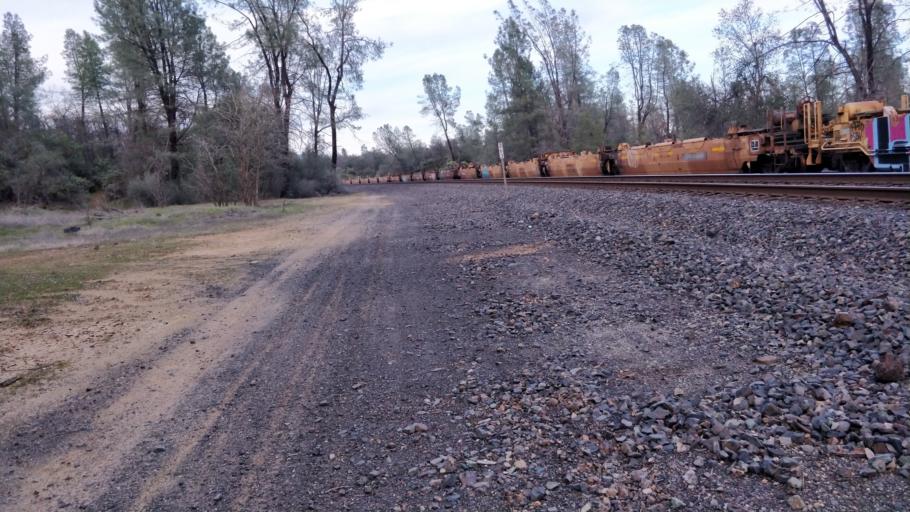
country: US
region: California
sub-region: Shasta County
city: Central Valley (historical)
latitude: 40.6443
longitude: -122.3936
